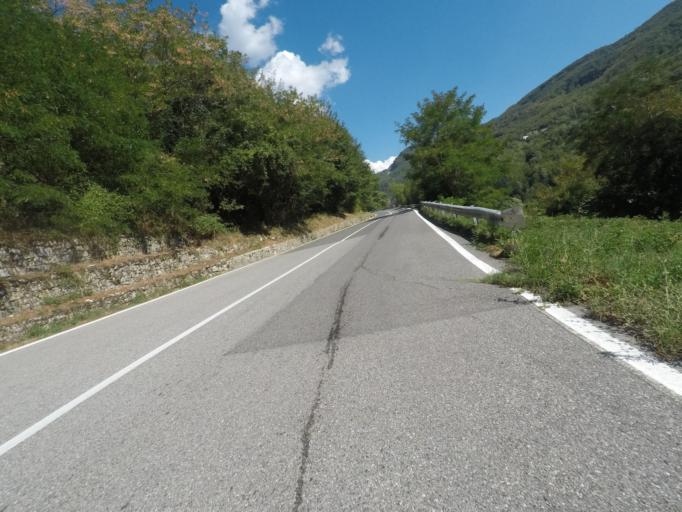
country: IT
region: Tuscany
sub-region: Provincia di Massa-Carrara
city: Fivizzano
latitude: 44.2515
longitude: 10.1745
